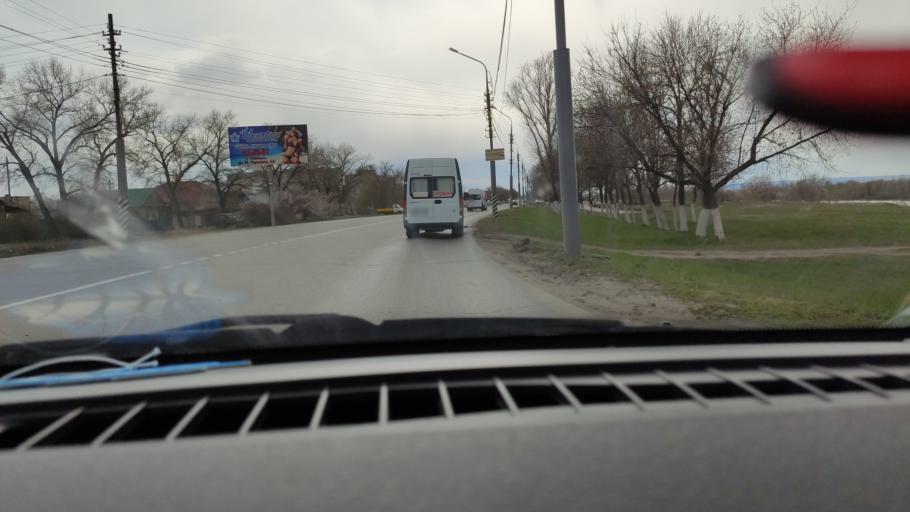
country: RU
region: Saratov
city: Engel's
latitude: 51.4477
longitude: 46.0778
